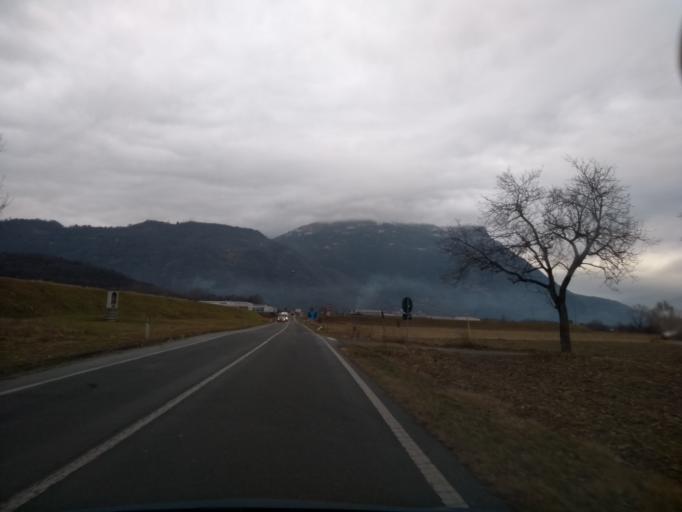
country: IT
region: Piedmont
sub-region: Provincia di Torino
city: Fiorano Canavese
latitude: 45.4722
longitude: 7.8376
